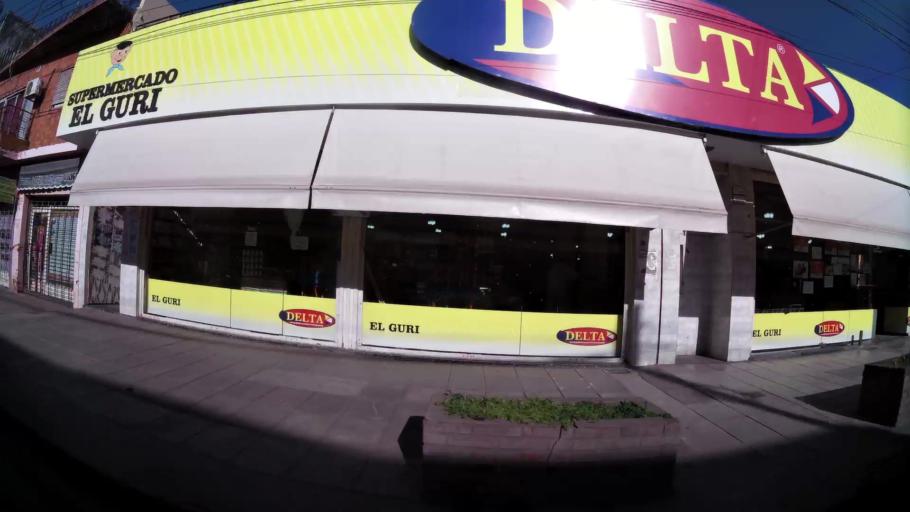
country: AR
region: Buenos Aires
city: Santa Catalina - Dique Lujan
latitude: -34.4916
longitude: -58.7272
